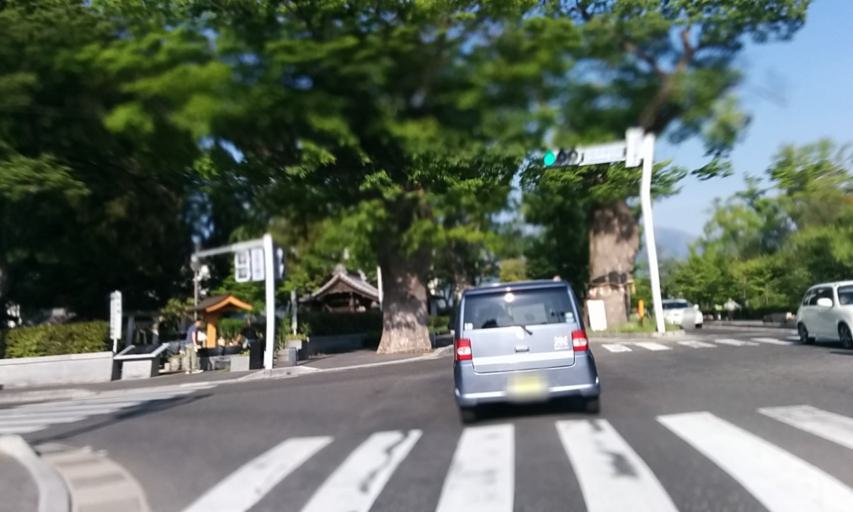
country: JP
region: Nagano
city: Matsumoto
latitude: 36.2396
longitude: 137.9685
